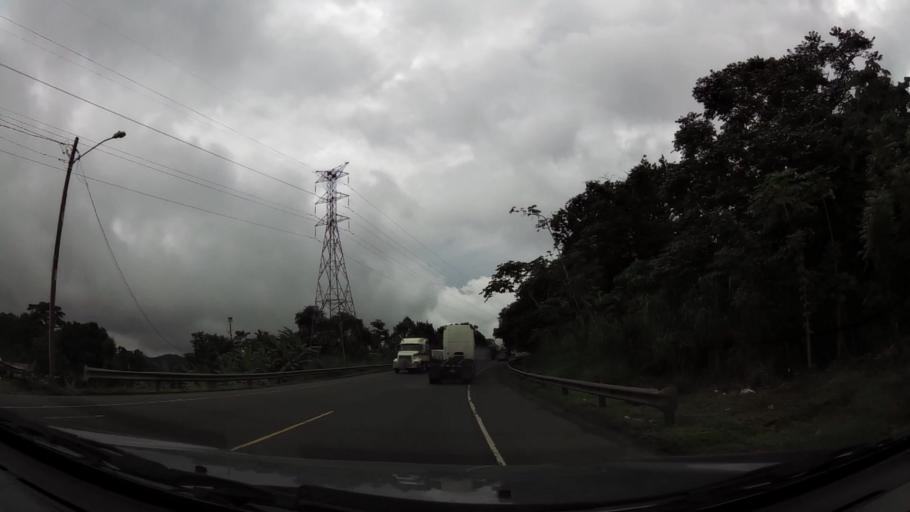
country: PA
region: Colon
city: Nuevo San Juan
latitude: 9.2025
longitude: -79.6264
